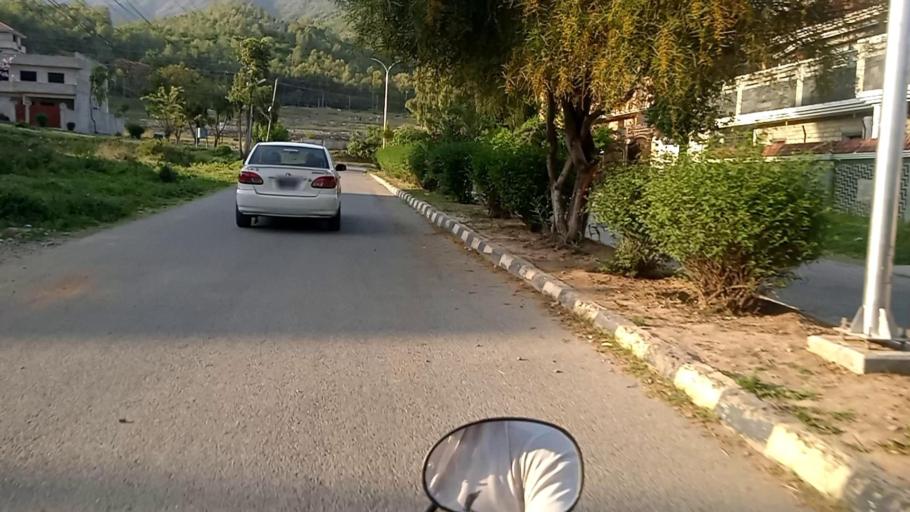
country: PK
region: Khyber Pakhtunkhwa
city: Mingora
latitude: 34.8321
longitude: 72.3422
